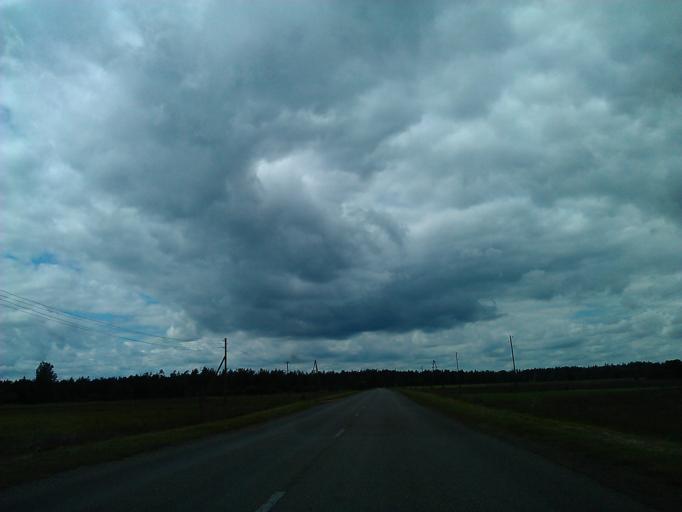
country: LV
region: Talsu Rajons
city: Stende
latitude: 57.0872
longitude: 22.3213
